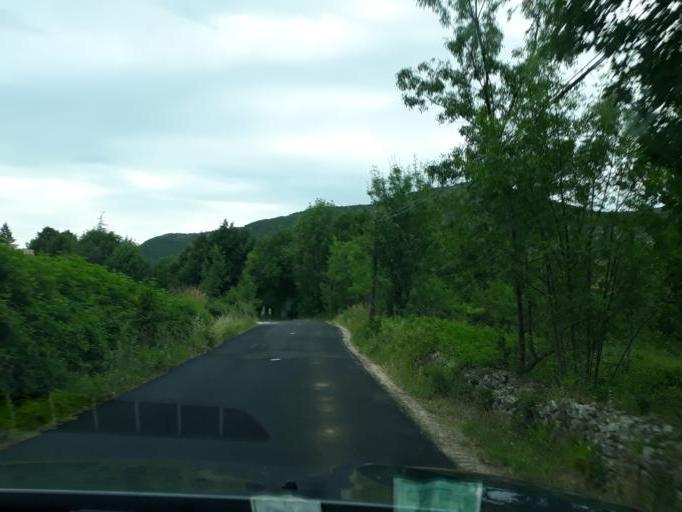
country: FR
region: Languedoc-Roussillon
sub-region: Departement de l'Herault
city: Lodeve
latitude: 43.7636
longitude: 3.3102
